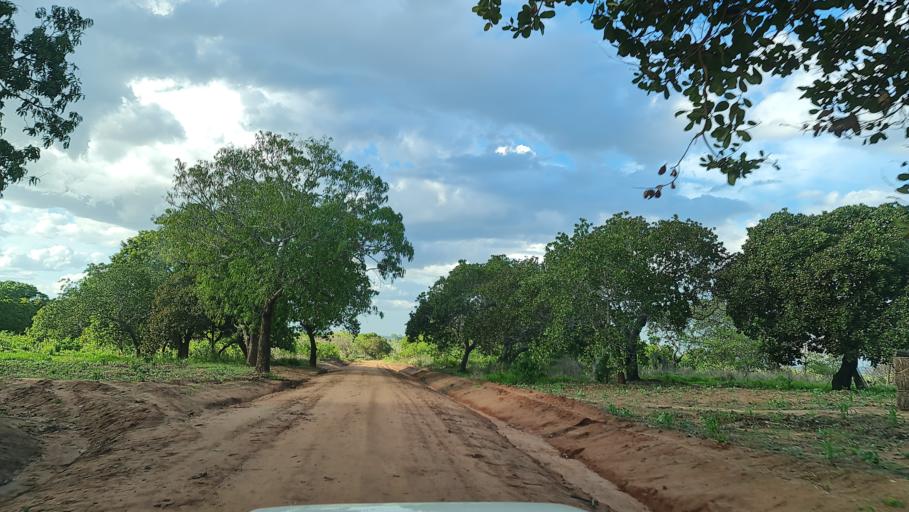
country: MZ
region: Cabo Delgado
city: Pemba
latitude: -13.5530
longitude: 40.1034
